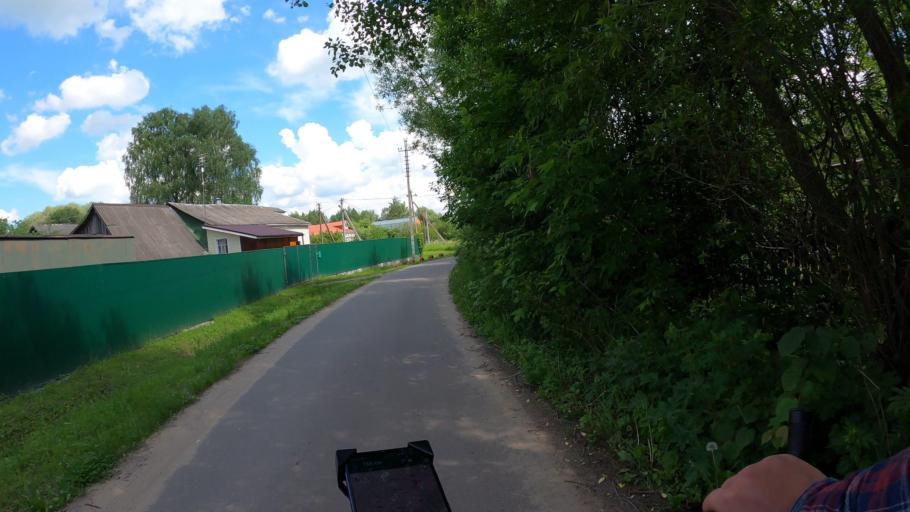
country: RU
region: Moskovskaya
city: Konobeyevo
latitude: 55.3972
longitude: 38.6783
